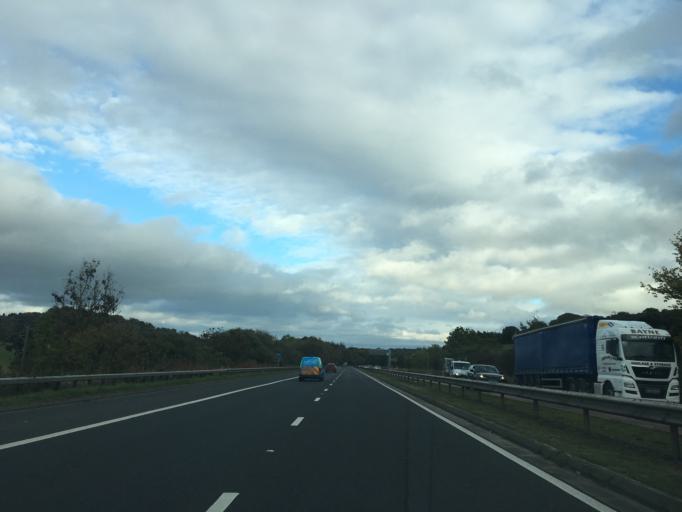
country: GB
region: Scotland
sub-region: Edinburgh
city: Queensferry
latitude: 55.9799
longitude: -3.3606
